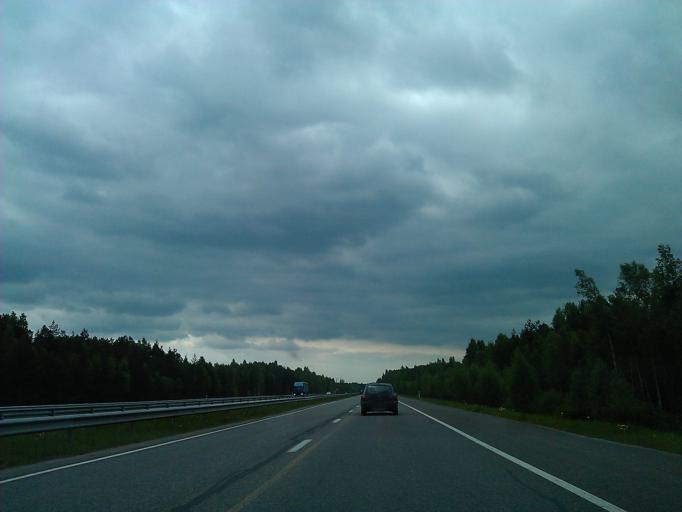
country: LV
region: Marupe
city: Marupe
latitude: 56.8647
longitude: 24.0654
